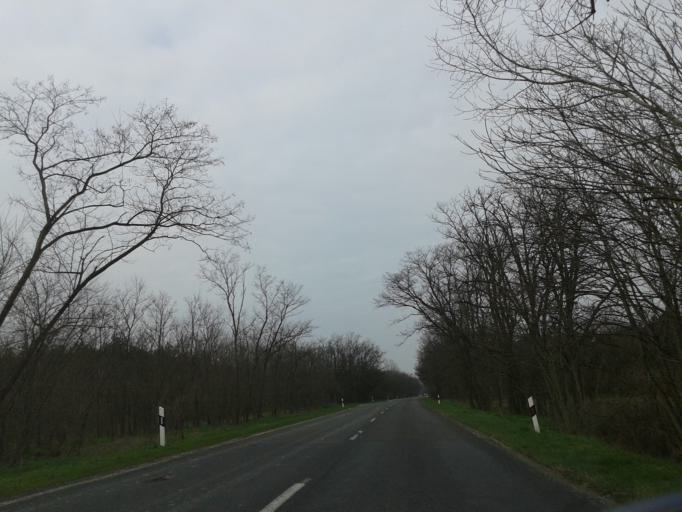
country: HU
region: Komarom-Esztergom
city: Acs
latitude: 47.7393
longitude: 17.9516
